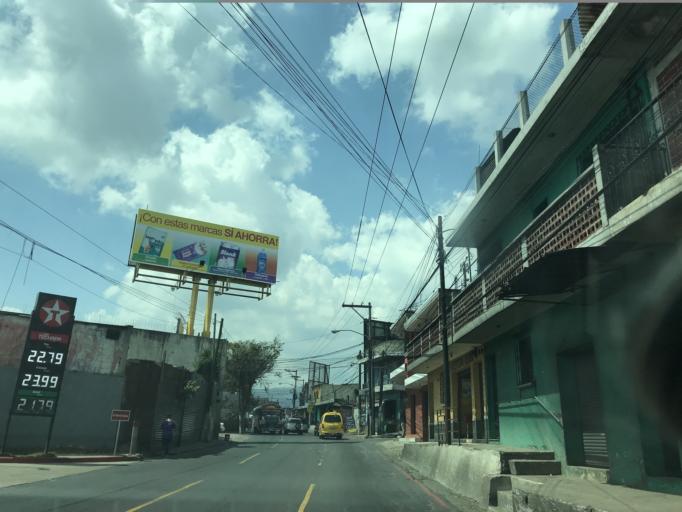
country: GT
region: Guatemala
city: Mixco
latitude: 14.6709
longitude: -90.5747
